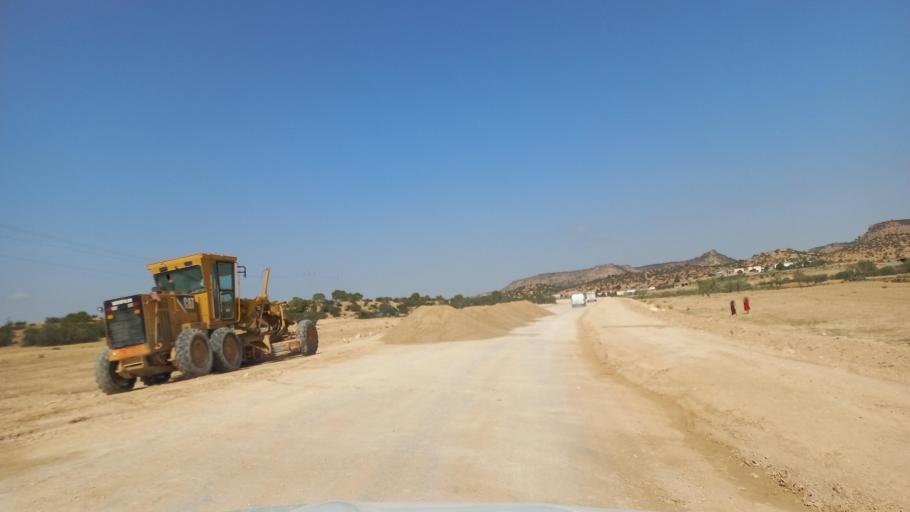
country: TN
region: Al Qasrayn
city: Sbiba
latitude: 35.4030
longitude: 8.9972
